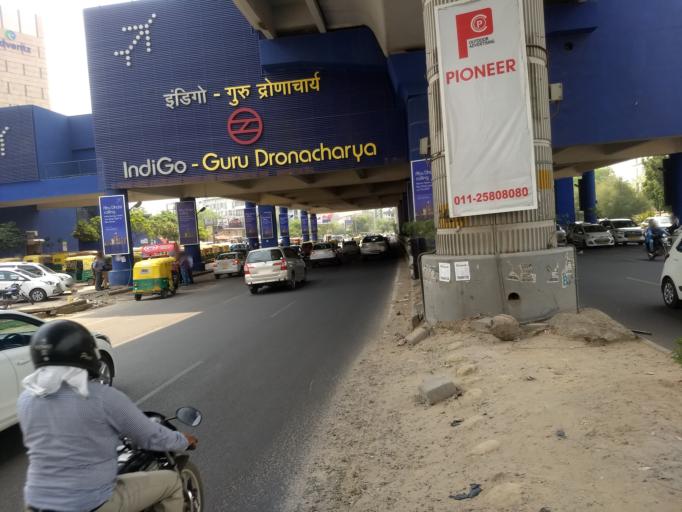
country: IN
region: Haryana
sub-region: Gurgaon
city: Gurgaon
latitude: 28.4822
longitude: 77.1028
